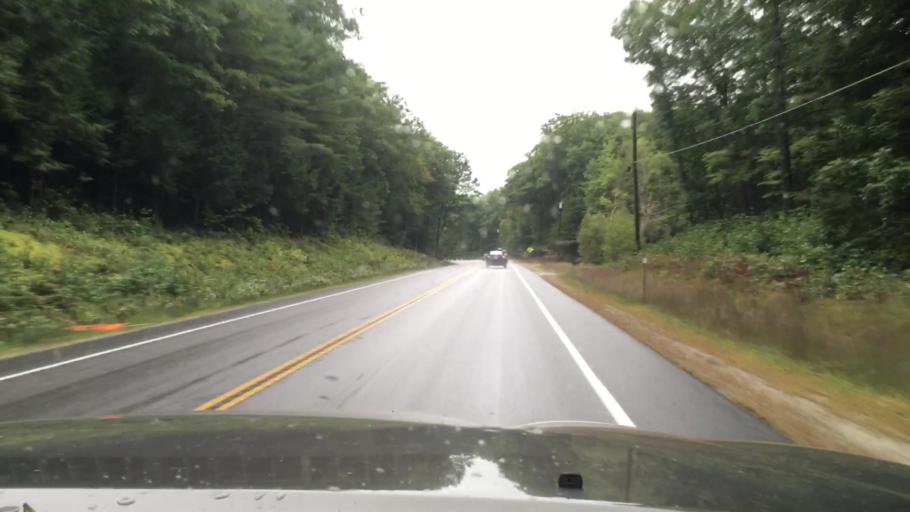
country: US
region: New Hampshire
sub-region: Hillsborough County
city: Antrim
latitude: 43.0757
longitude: -72.0112
